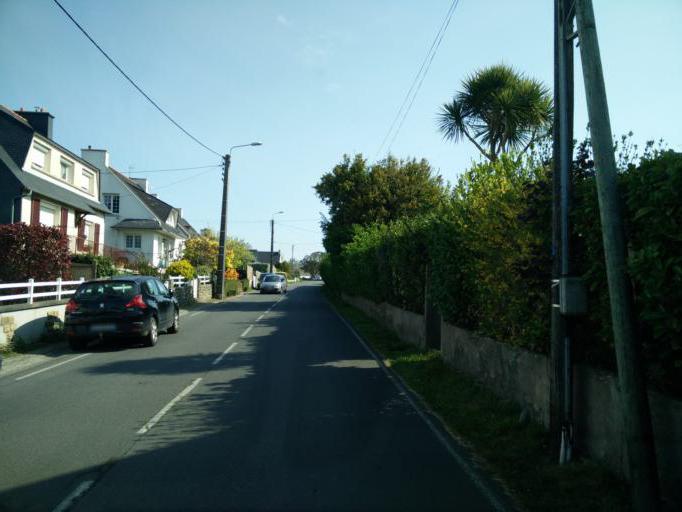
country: FR
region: Brittany
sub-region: Departement du Finistere
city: Crozon
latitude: 48.2431
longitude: -4.4842
